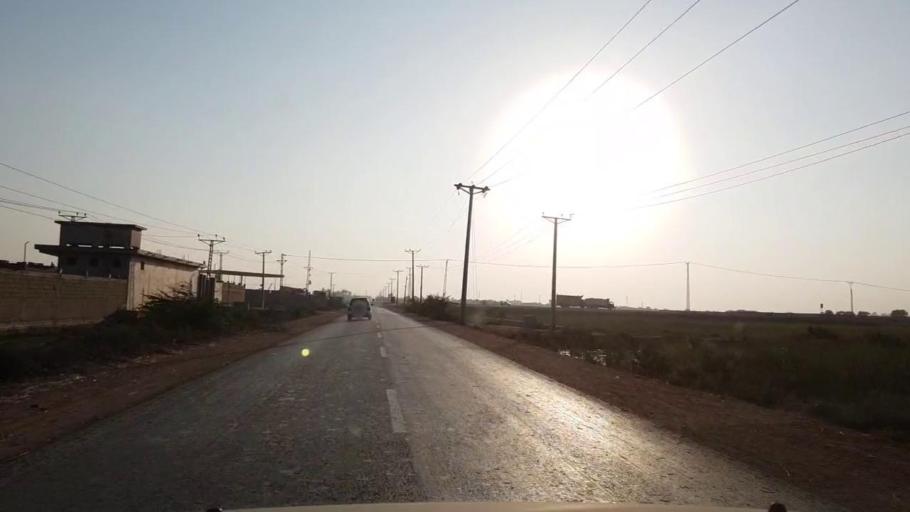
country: PK
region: Sindh
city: Daro Mehar
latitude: 24.6159
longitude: 68.0910
